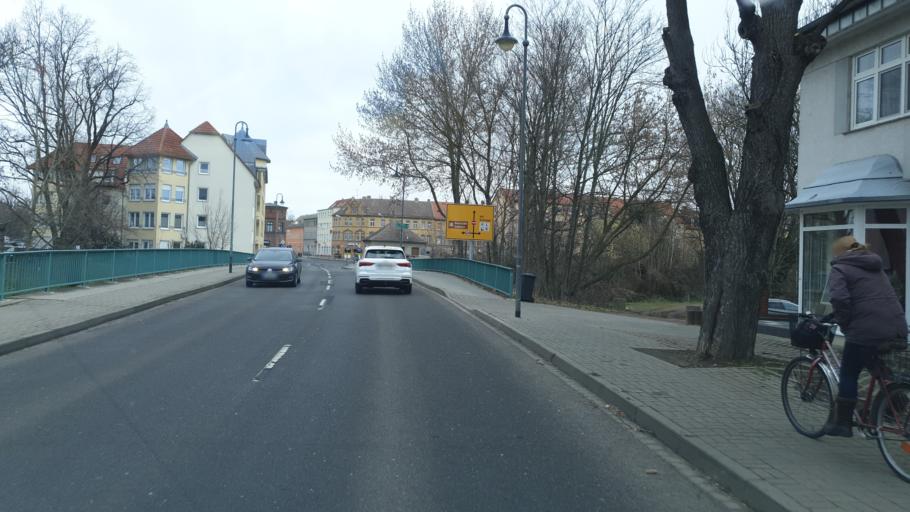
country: DE
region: Saxony
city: Delitzsch
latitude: 51.5206
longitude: 12.3371
